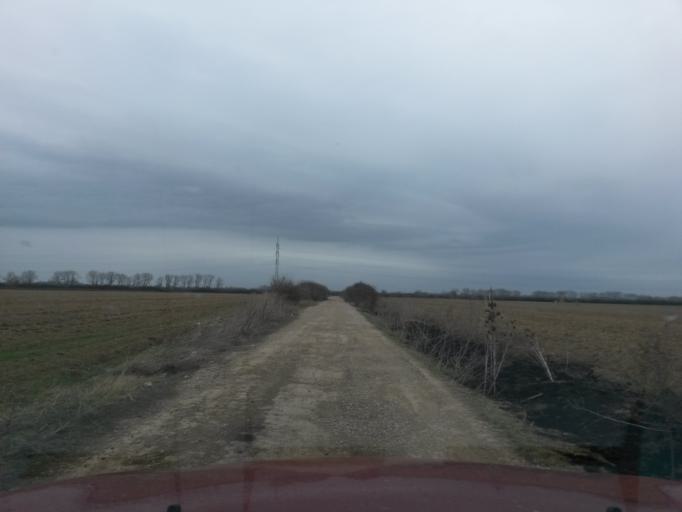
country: SK
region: Kosicky
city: Michalovce
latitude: 48.6915
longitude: 21.8907
